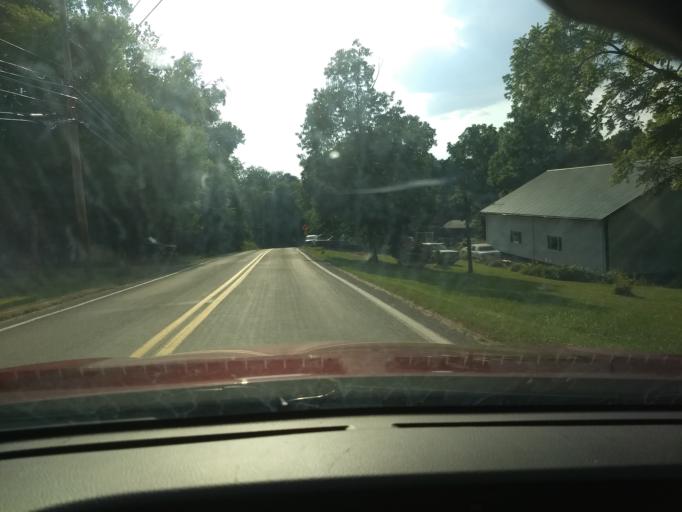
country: US
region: Pennsylvania
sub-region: Westmoreland County
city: Lower Burrell
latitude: 40.5373
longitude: -79.7590
